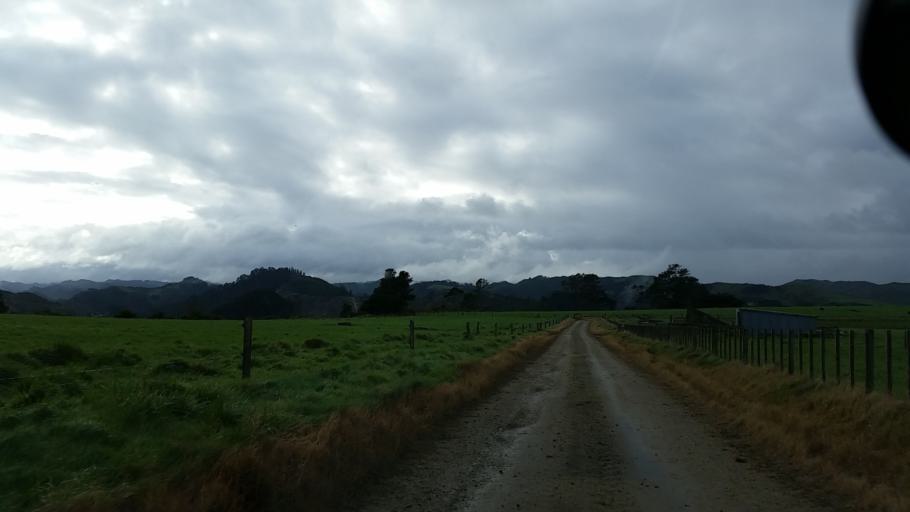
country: NZ
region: Taranaki
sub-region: South Taranaki District
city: Patea
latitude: -39.7240
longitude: 174.7173
